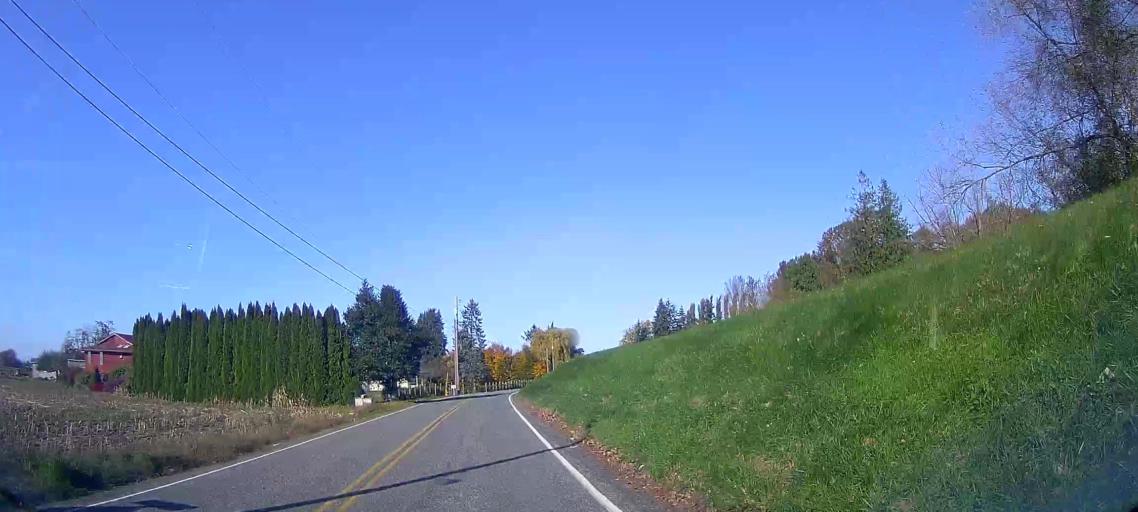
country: US
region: Washington
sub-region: Skagit County
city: Mount Vernon
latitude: 48.4082
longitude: -122.3682
